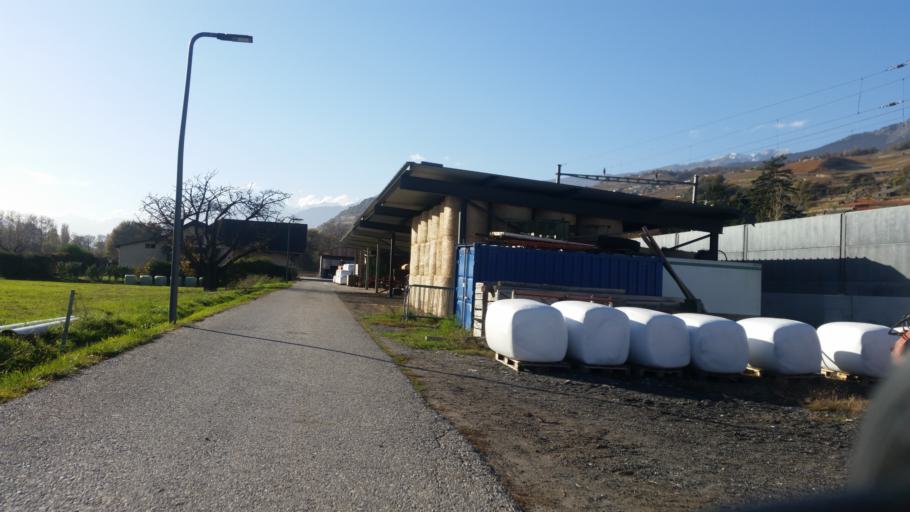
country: CH
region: Valais
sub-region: Sion District
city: Saint-Leonard
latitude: 46.2493
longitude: 7.4098
